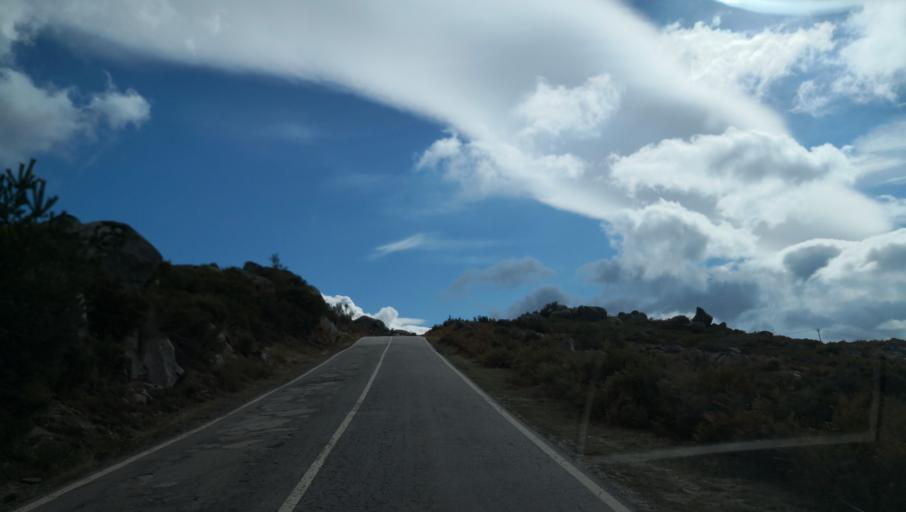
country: PT
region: Vila Real
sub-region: Vila Real
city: Vila Real
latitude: 41.3604
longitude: -7.7966
